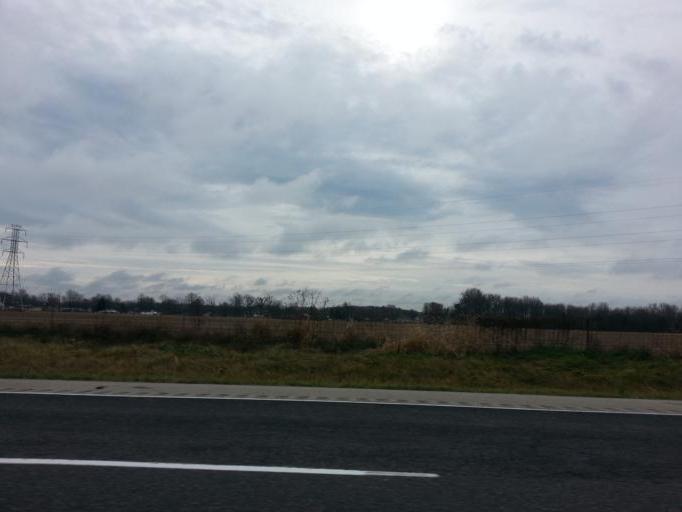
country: US
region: Indiana
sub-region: Ripley County
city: Batesville
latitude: 39.3166
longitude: -85.3299
